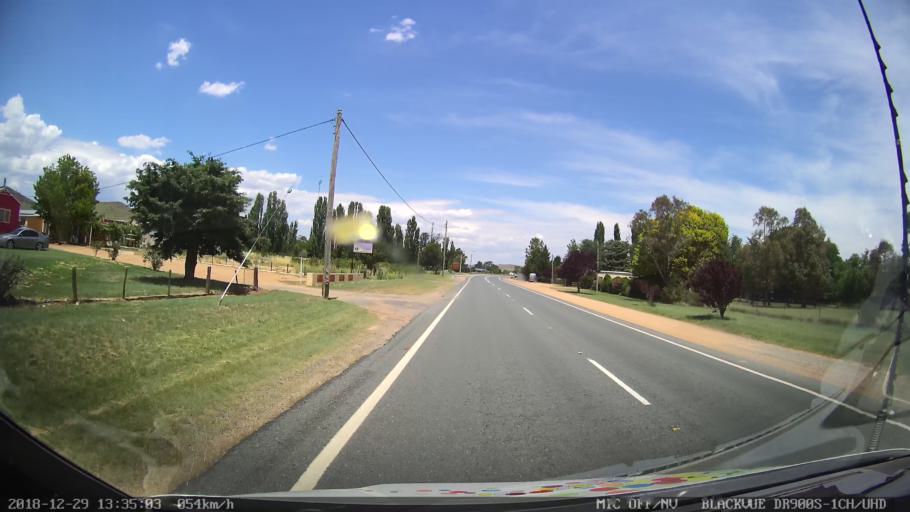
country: AU
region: New South Wales
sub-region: Cooma-Monaro
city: Cooma
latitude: -35.9573
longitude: 149.1493
